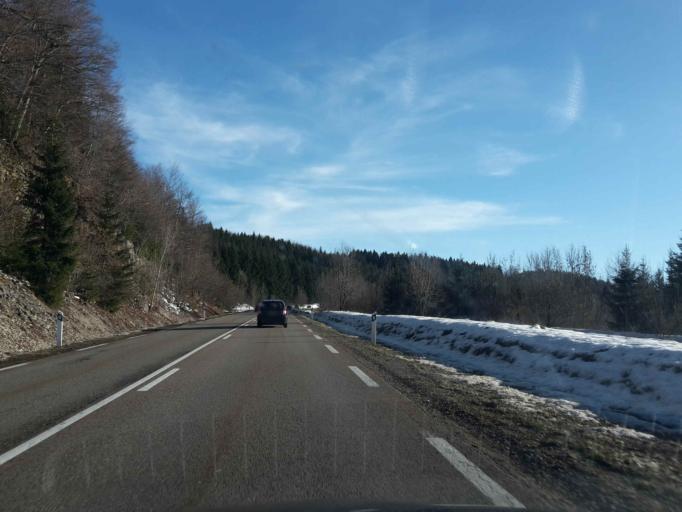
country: FR
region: Franche-Comte
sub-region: Departement du Doubs
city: Doubs
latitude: 47.0000
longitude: 6.3277
